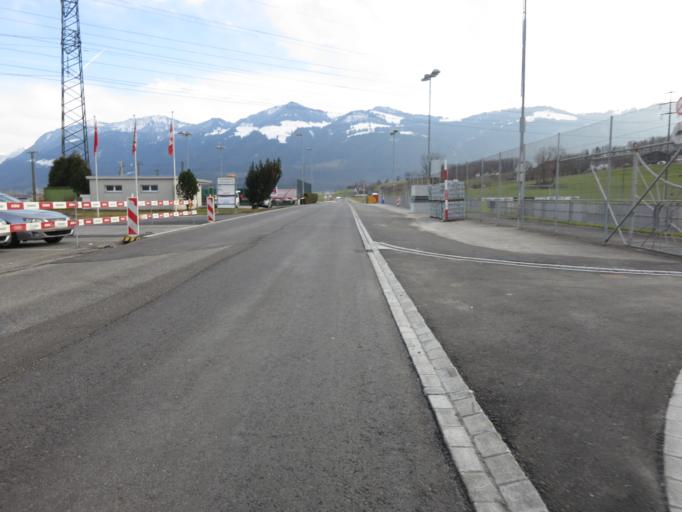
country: CH
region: Schwyz
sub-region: Bezirk March
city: Tuggen
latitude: 47.1965
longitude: 8.9426
